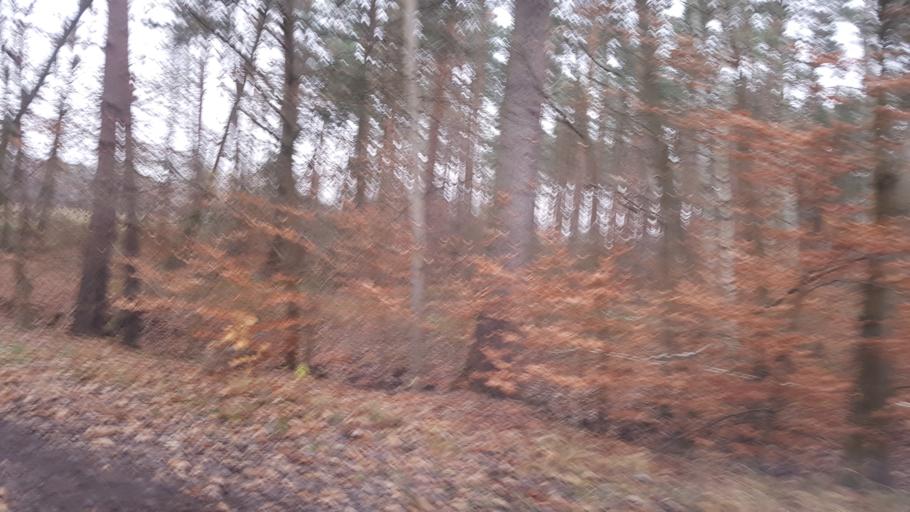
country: DE
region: Brandenburg
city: Doberlug-Kirchhain
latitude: 51.6274
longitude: 13.5293
